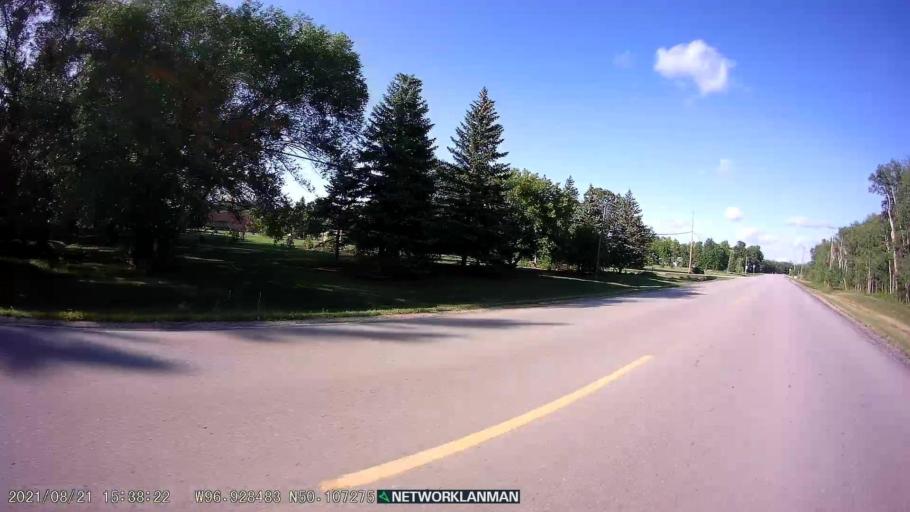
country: CA
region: Manitoba
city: Selkirk
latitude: 50.1073
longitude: -96.9284
